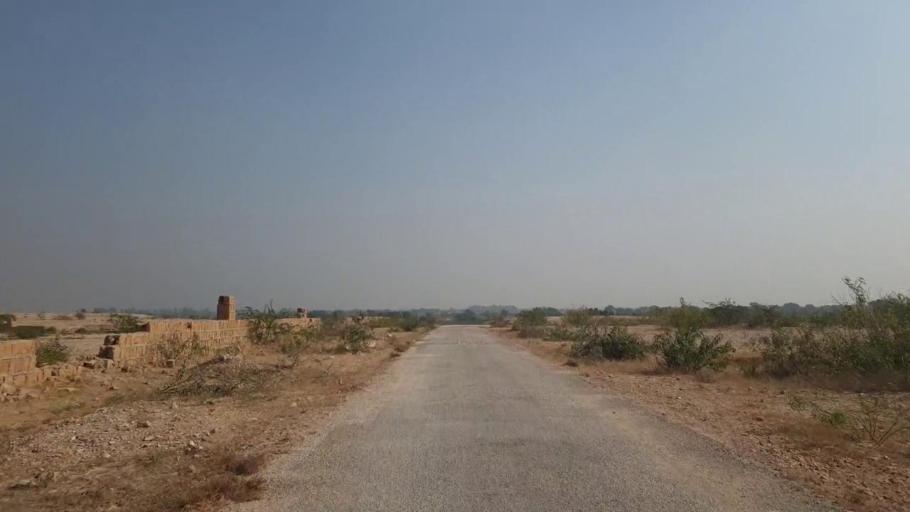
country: PK
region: Sindh
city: Kotri
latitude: 25.3197
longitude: 68.2679
